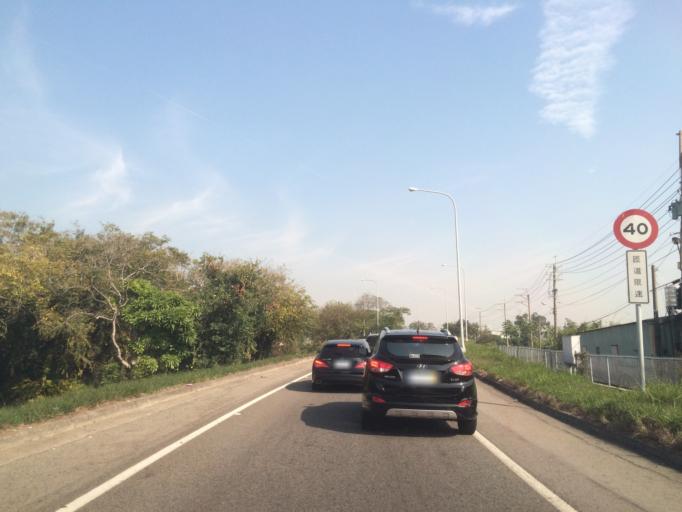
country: TW
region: Taiwan
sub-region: Taichung City
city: Taichung
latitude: 24.2039
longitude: 120.6574
